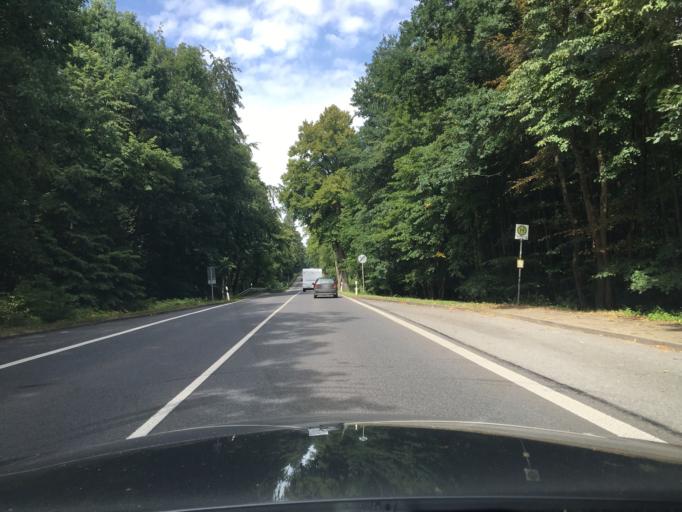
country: DE
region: Brandenburg
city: Furstenberg
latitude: 53.2439
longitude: 13.1110
